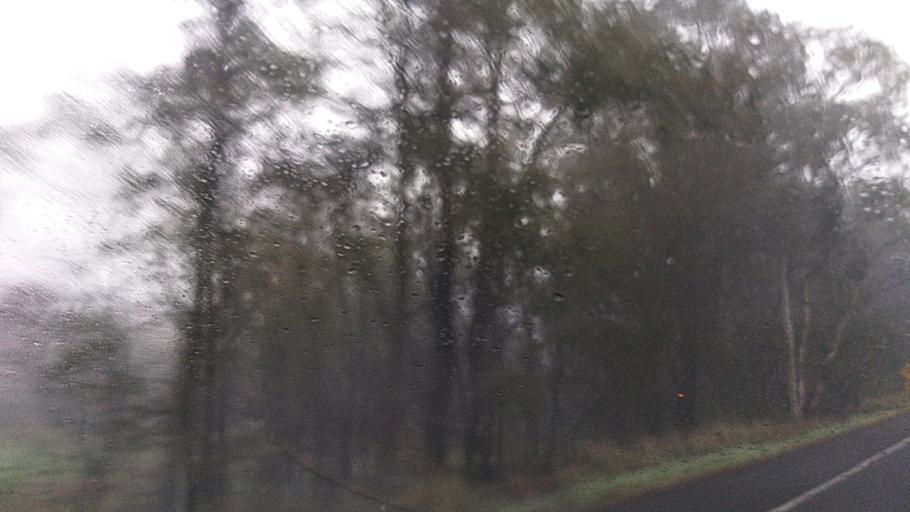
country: AU
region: New South Wales
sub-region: Wollondilly
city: Douglas Park
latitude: -34.2411
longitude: 150.7281
